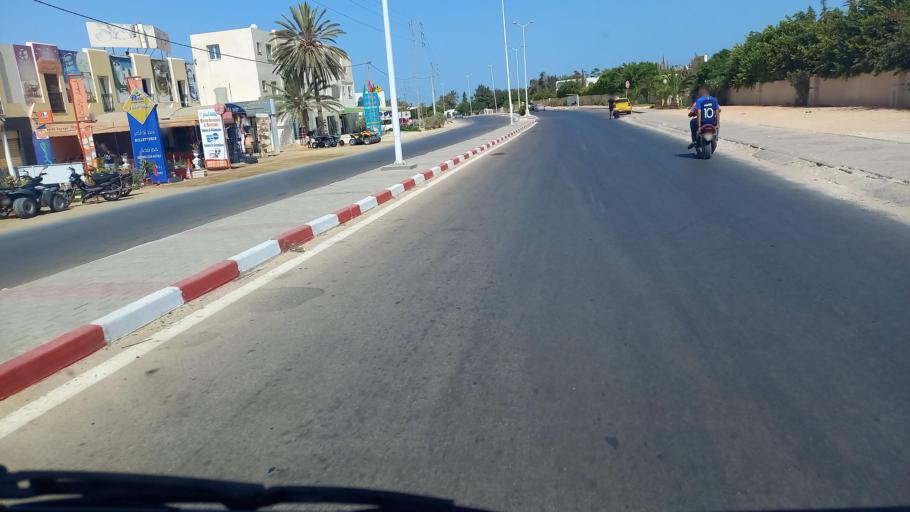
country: TN
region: Madanin
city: Midoun
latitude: 33.8583
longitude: 10.9749
